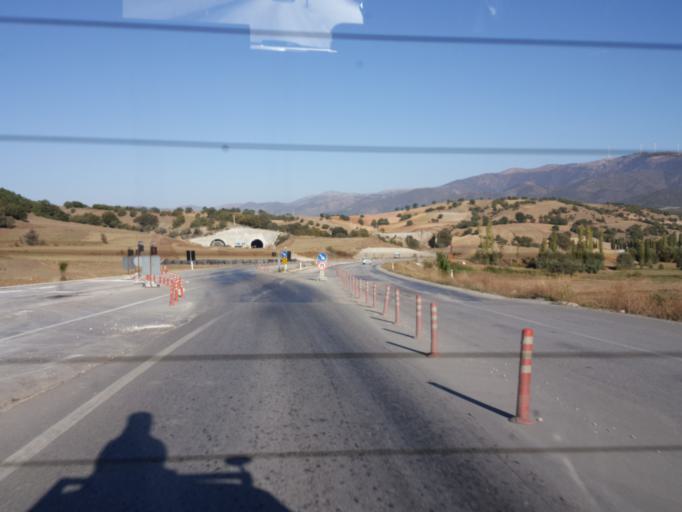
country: TR
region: Amasya
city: Ezinepazari
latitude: 40.5529
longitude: 36.1414
